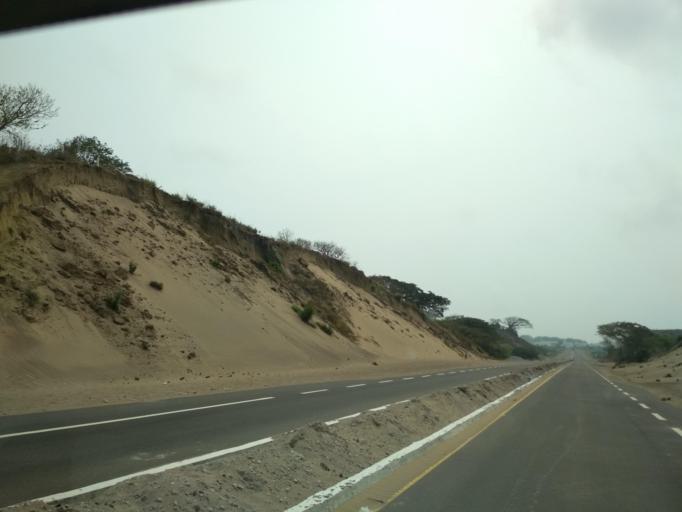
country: MX
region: Veracruz
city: Anton Lizardo
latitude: 19.0428
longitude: -95.9914
